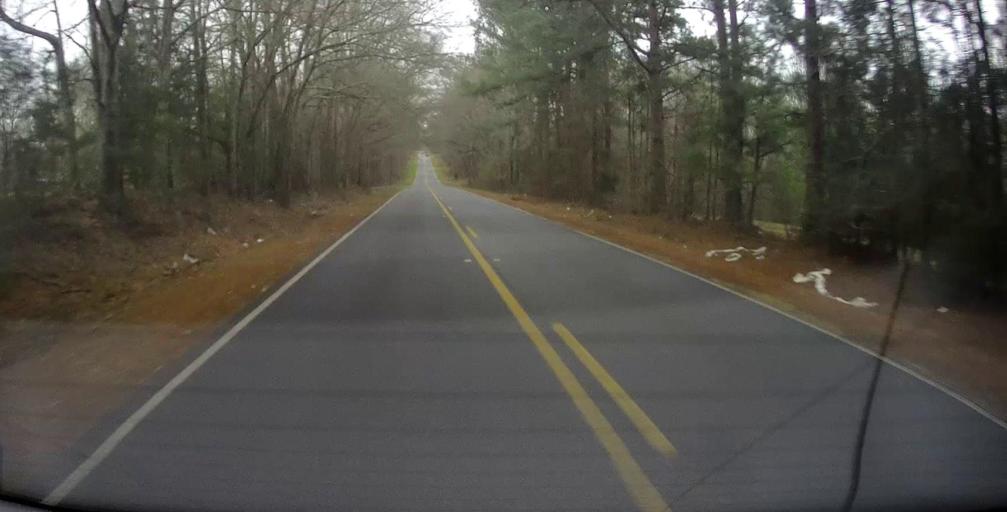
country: US
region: Georgia
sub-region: Pike County
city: Zebulon
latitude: 33.0620
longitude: -84.3253
